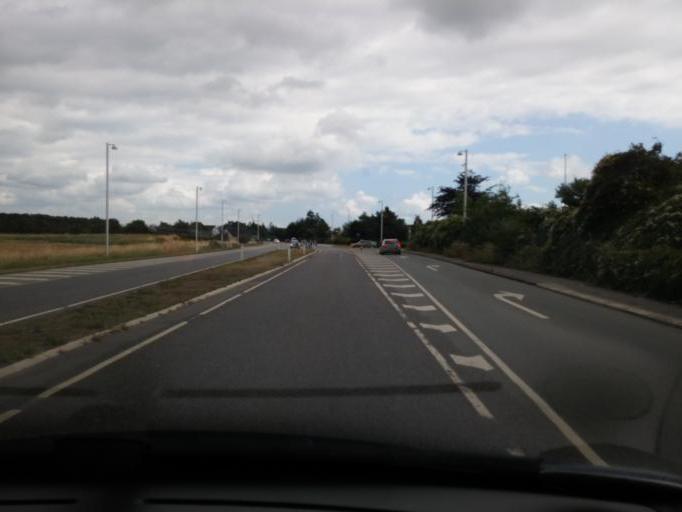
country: DK
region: South Denmark
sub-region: Langeland Kommune
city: Rudkobing
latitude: 54.9442
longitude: 10.7202
